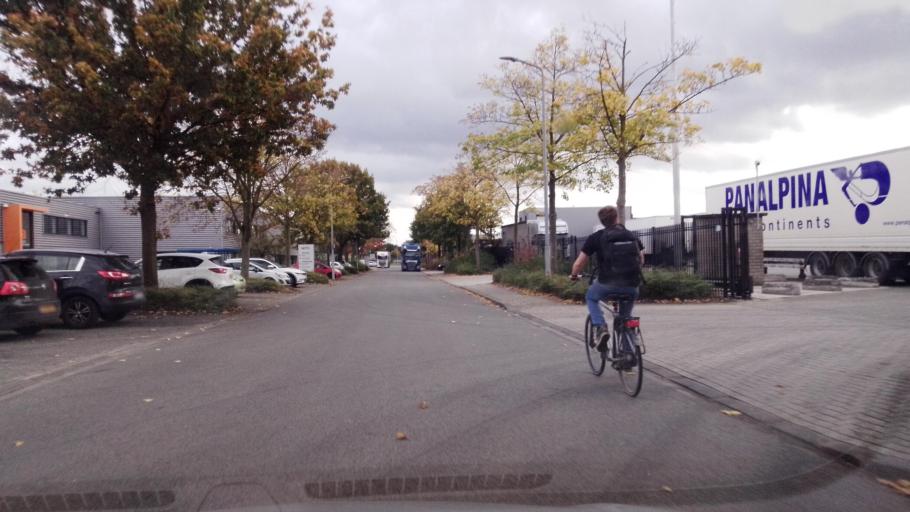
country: NL
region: Limburg
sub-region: Gemeente Venlo
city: Venlo
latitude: 51.3850
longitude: 6.1553
